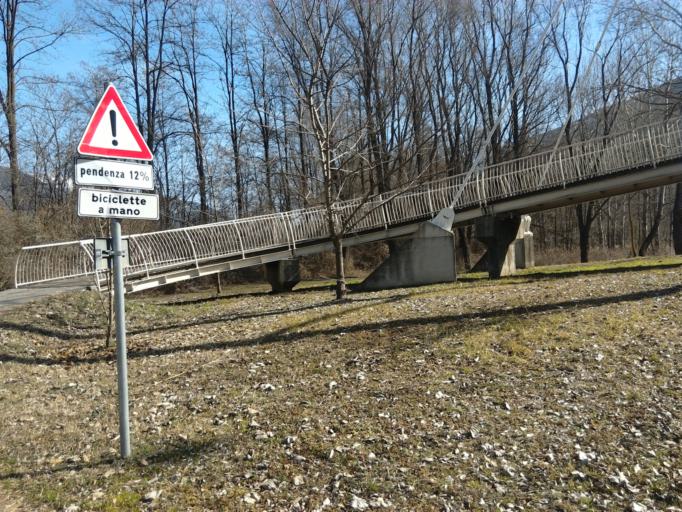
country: IT
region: Lombardy
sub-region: Provincia di Sondrio
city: Torchione-Moia
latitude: 46.1588
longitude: 9.8605
